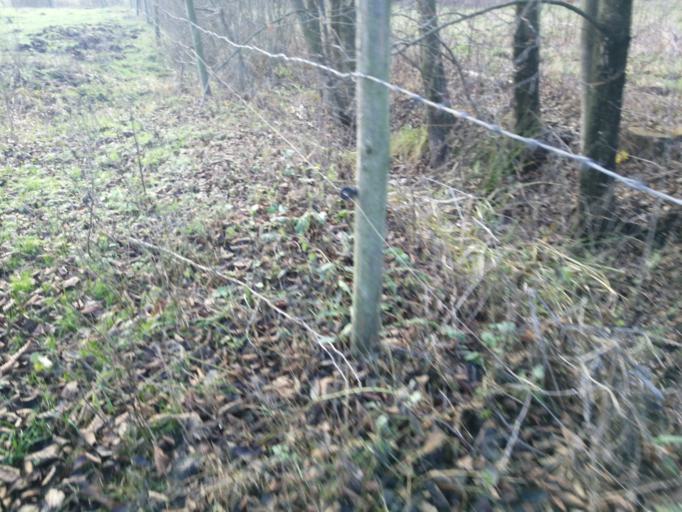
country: PL
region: Warmian-Masurian Voivodeship
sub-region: Powiat dzialdowski
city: Rybno
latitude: 53.4130
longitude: 19.9080
